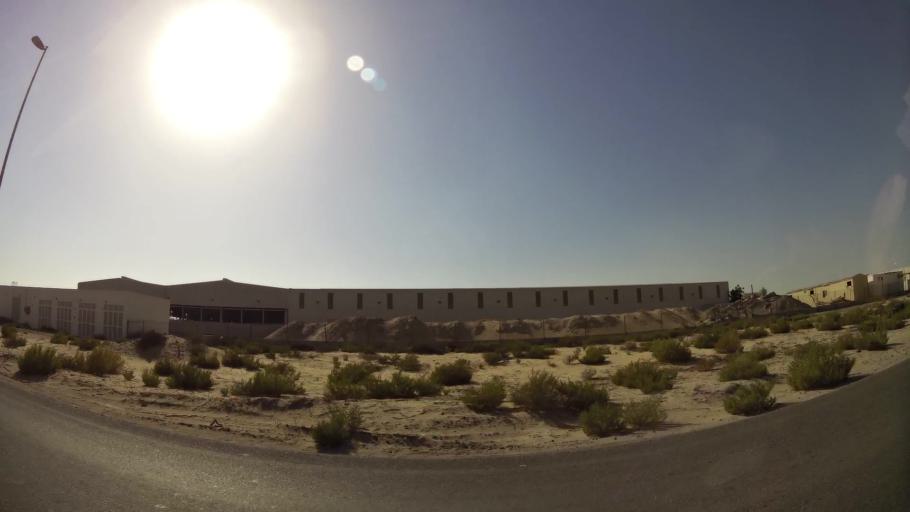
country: AE
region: Dubai
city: Dubai
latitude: 24.9921
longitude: 55.1221
